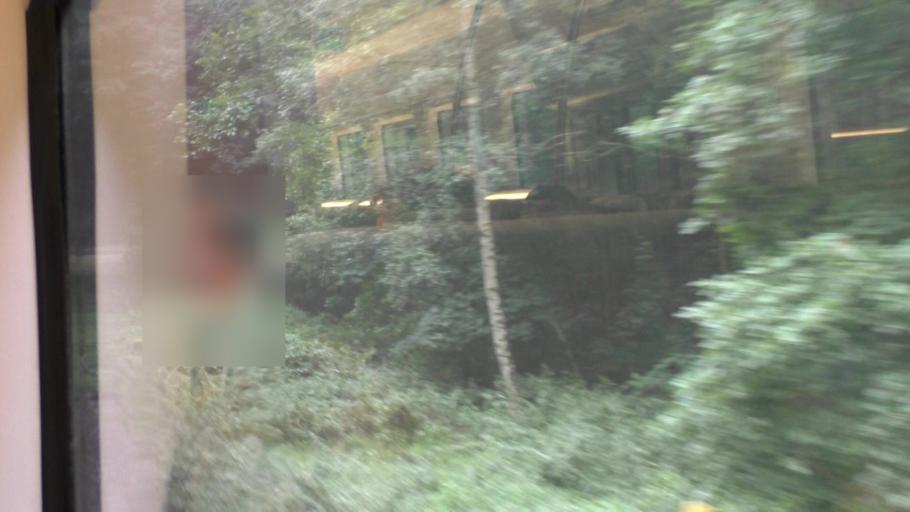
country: DE
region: Saxony
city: Neugersdorf
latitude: 50.9896
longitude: 14.6187
